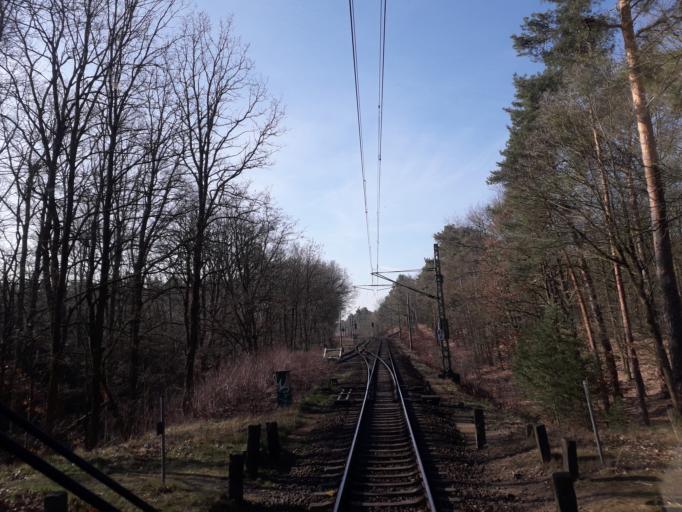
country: DE
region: Brandenburg
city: Michendorf
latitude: 52.3118
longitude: 12.9680
